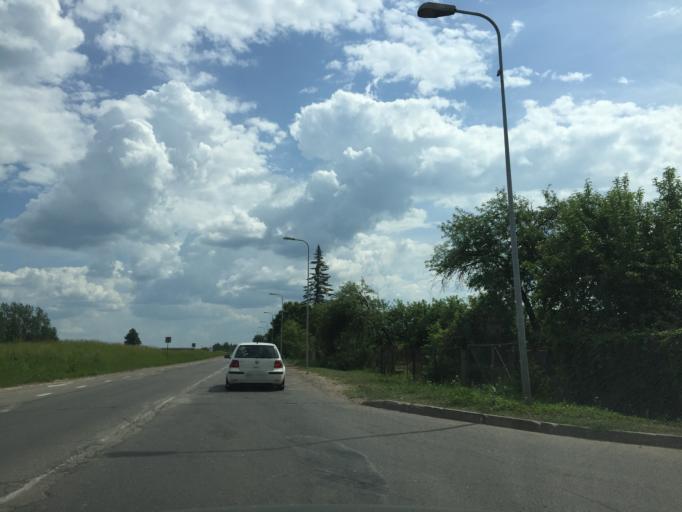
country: LV
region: Jekabpils Rajons
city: Jekabpils
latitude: 56.5101
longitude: 25.8748
